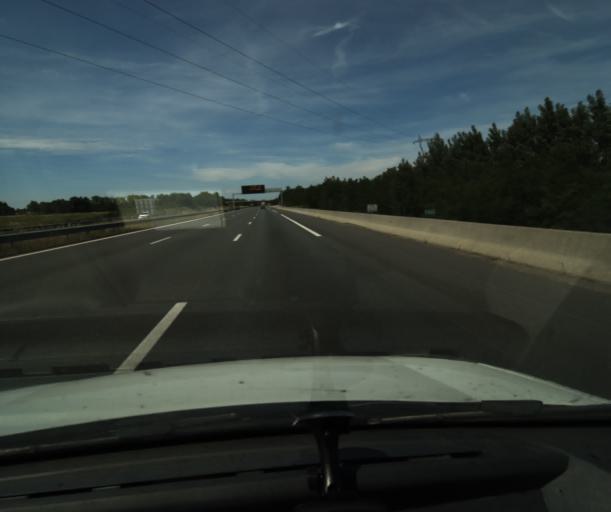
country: FR
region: Midi-Pyrenees
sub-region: Departement du Tarn-et-Garonne
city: Campsas
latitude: 43.8949
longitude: 1.3170
